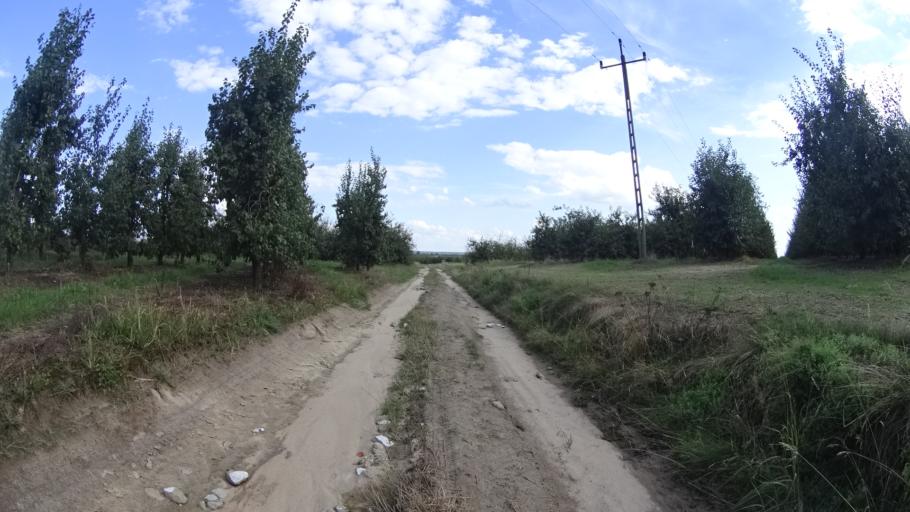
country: PL
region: Masovian Voivodeship
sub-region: Powiat bialobrzeski
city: Wysmierzyce
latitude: 51.6681
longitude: 20.8090
